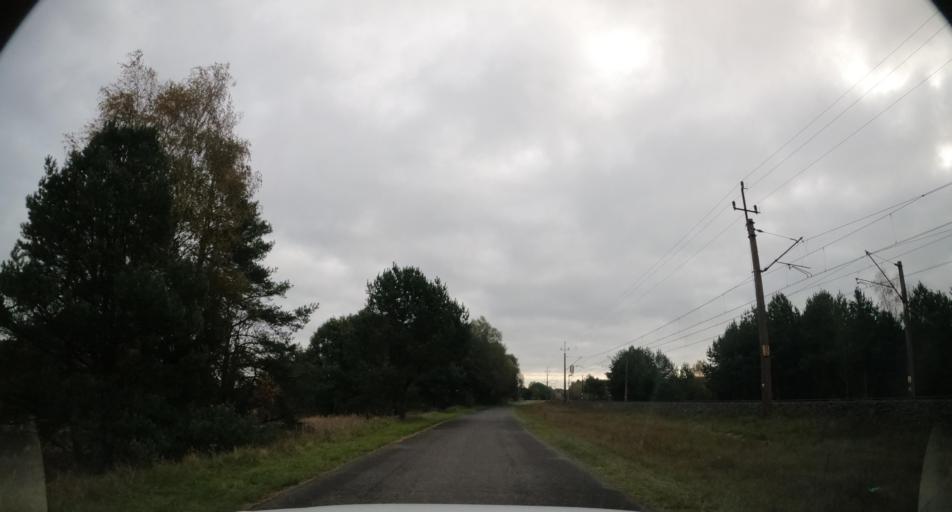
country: PL
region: West Pomeranian Voivodeship
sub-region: Powiat kamienski
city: Miedzyzdroje
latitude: 53.9257
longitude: 14.5497
